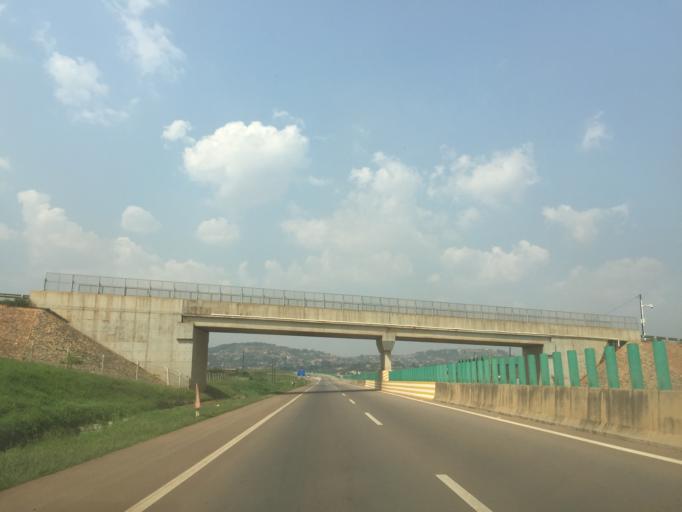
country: UG
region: Central Region
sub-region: Wakiso District
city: Kajansi
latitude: 0.2083
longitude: 32.5293
